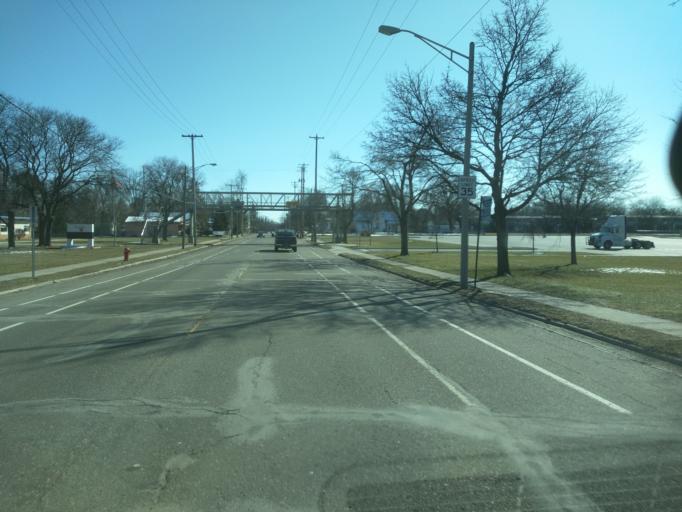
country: US
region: Michigan
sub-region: Ingham County
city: Lansing
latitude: 42.6893
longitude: -84.5824
